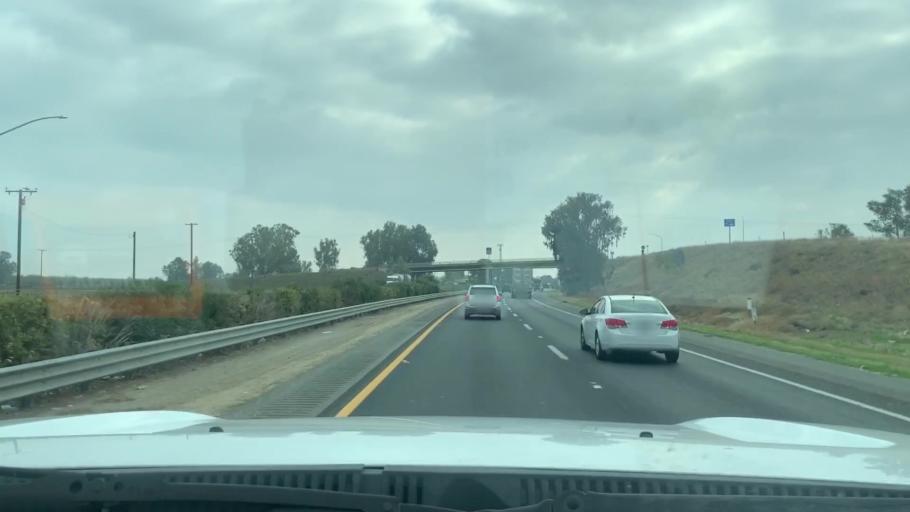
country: US
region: California
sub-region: Tulare County
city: Pixley
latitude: 36.0095
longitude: -119.3026
